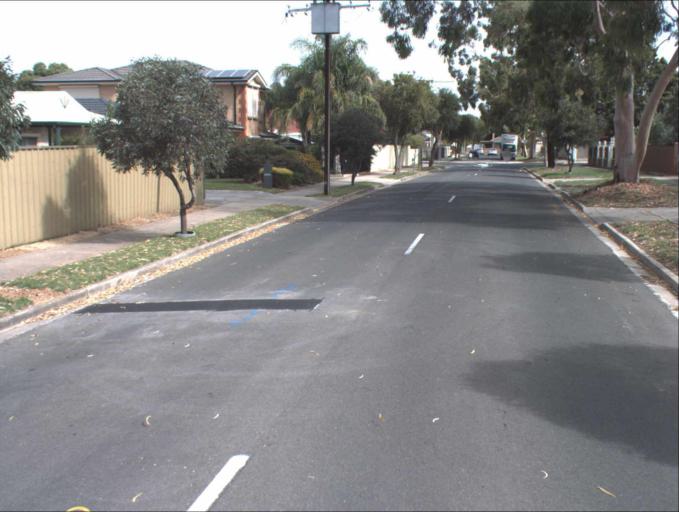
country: AU
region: South Australia
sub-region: Port Adelaide Enfield
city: Blair Athol
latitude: -34.8644
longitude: 138.5896
